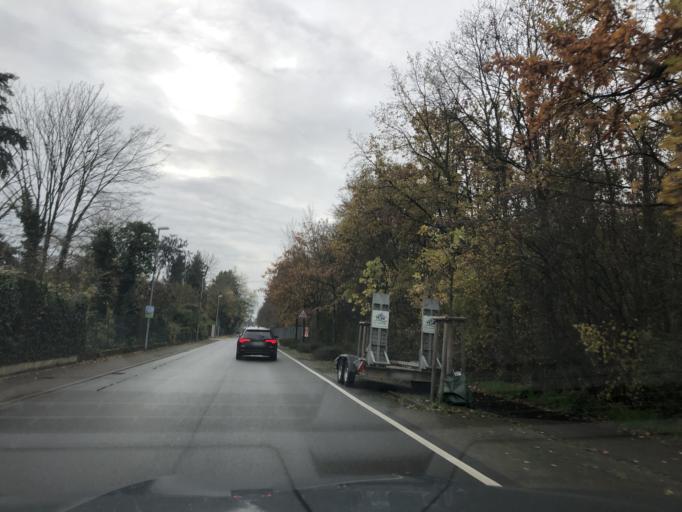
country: DE
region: Baden-Wuerttemberg
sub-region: Karlsruhe Region
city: Walldorf
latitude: 49.3142
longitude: 8.6445
